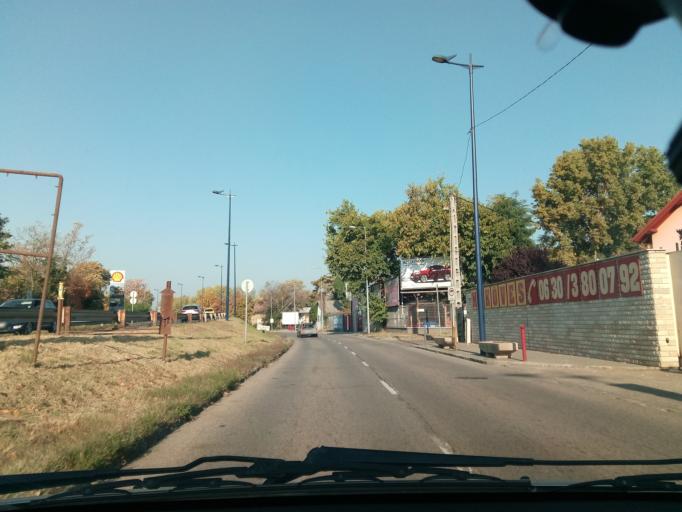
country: HU
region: Budapest
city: Budapest XVIII. keruelet
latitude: 47.4615
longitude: 19.1692
